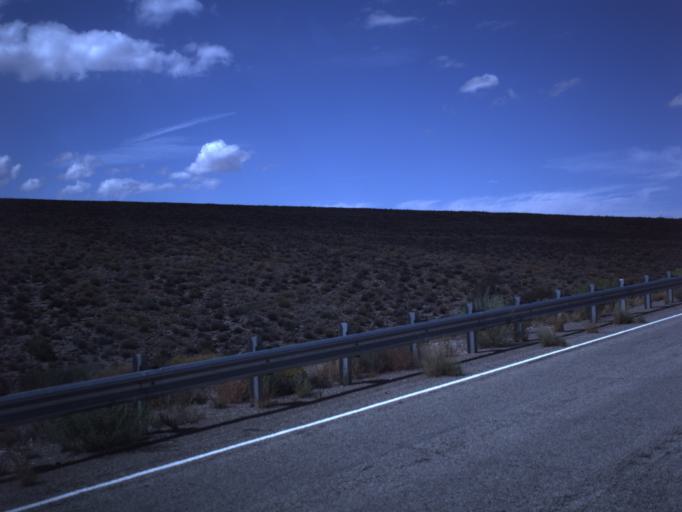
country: US
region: Utah
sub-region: San Juan County
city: Blanding
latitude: 37.2823
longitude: -109.6889
